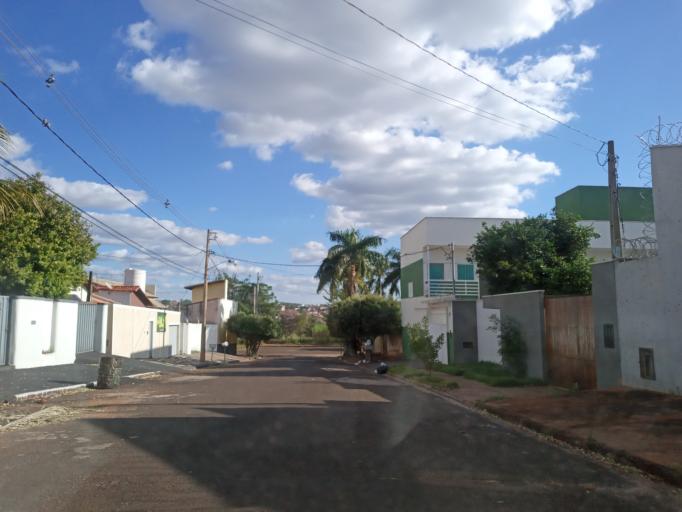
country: BR
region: Minas Gerais
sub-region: Ituiutaba
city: Ituiutaba
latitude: -18.9726
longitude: -49.4446
